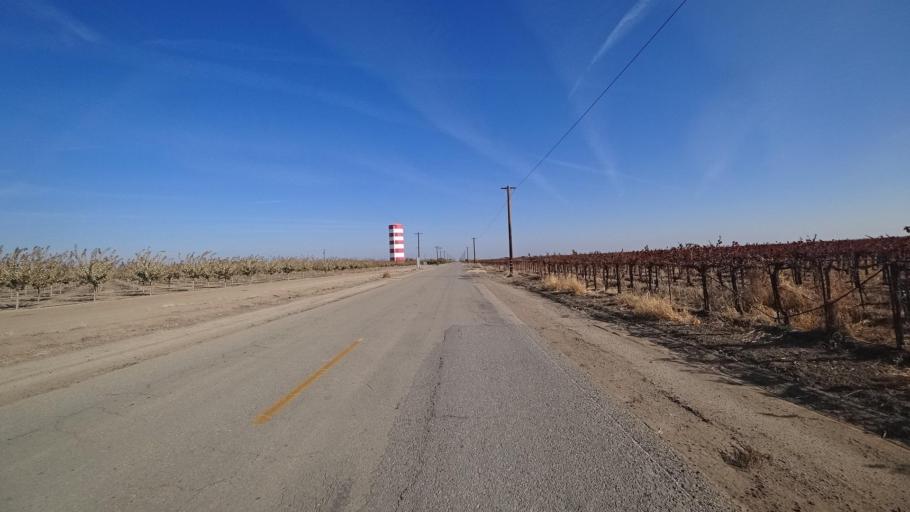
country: US
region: California
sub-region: Kern County
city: Wasco
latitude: 35.7032
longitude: -119.3417
